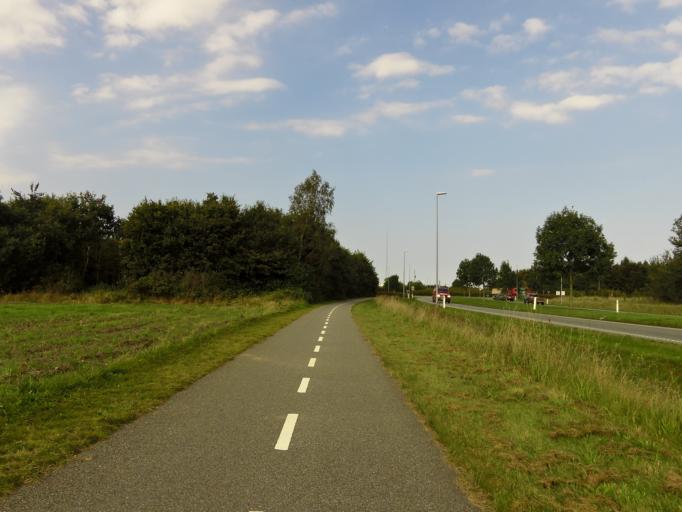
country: DK
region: South Denmark
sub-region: Vejen Kommune
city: Vejen
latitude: 55.4608
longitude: 9.1339
